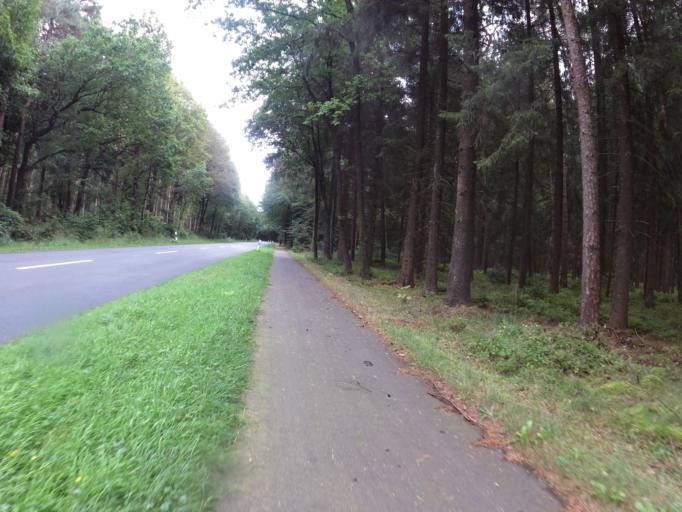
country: DE
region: Lower Saxony
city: Oerel
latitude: 53.4968
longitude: 9.0096
